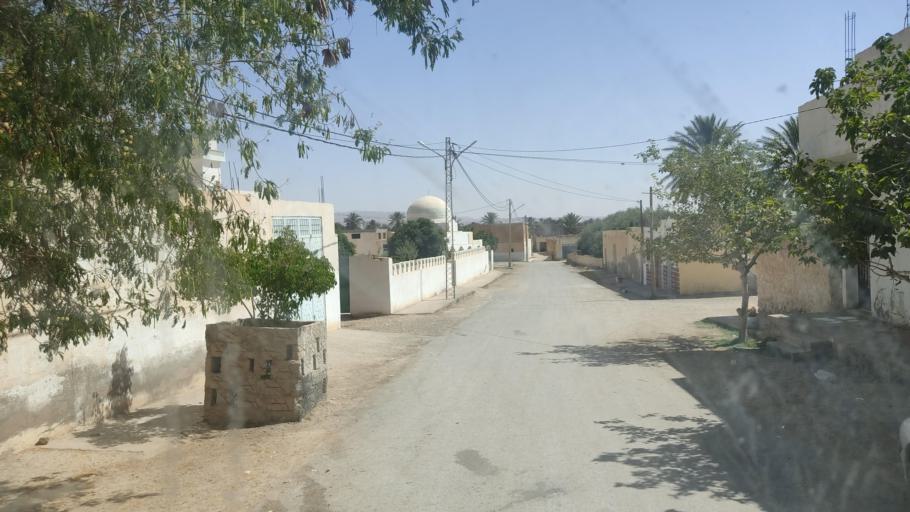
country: TN
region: Gafsa
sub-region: Gafsa Municipality
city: Gafsa
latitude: 34.3367
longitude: 8.9210
